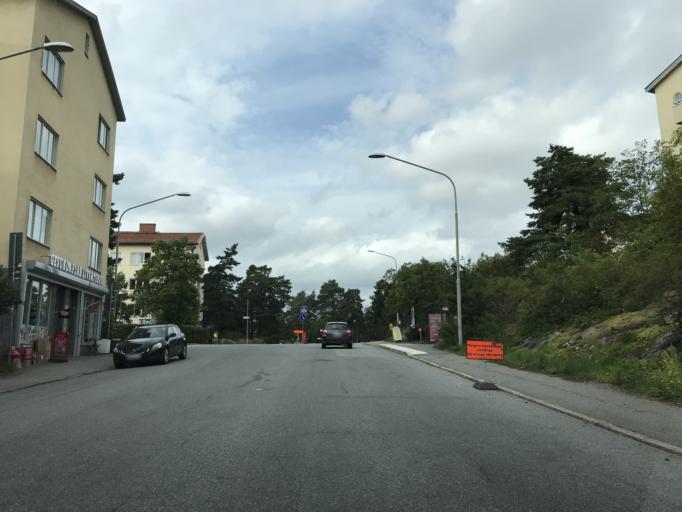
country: SE
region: Stockholm
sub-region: Sundbybergs Kommun
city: Sundbyberg
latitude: 59.3379
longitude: 17.9821
